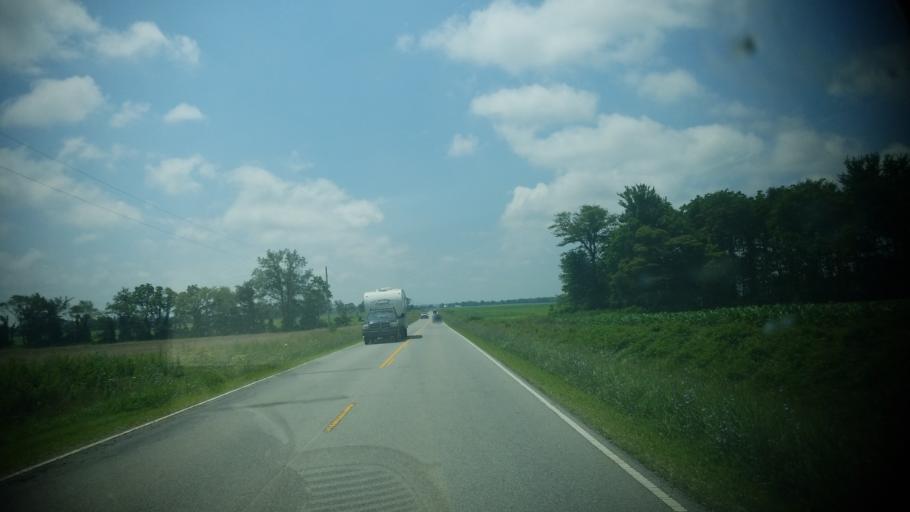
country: US
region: Illinois
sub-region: Wayne County
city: Fairfield
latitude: 38.5024
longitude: -88.3485
